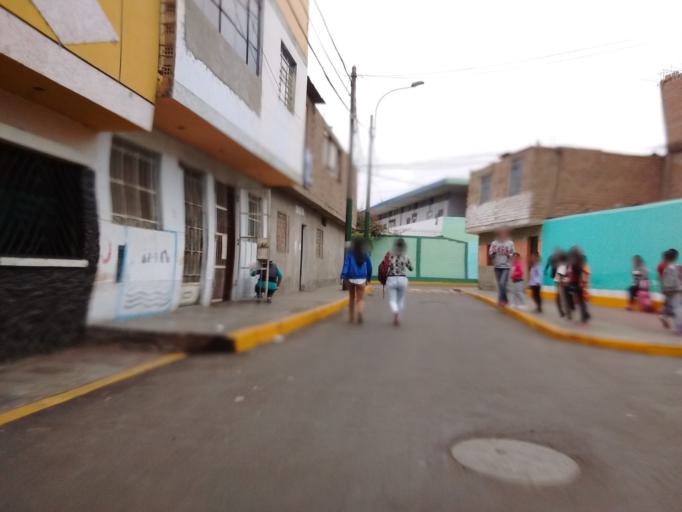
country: PE
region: Callao
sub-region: Callao
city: Callao
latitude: -12.0448
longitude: -77.0975
